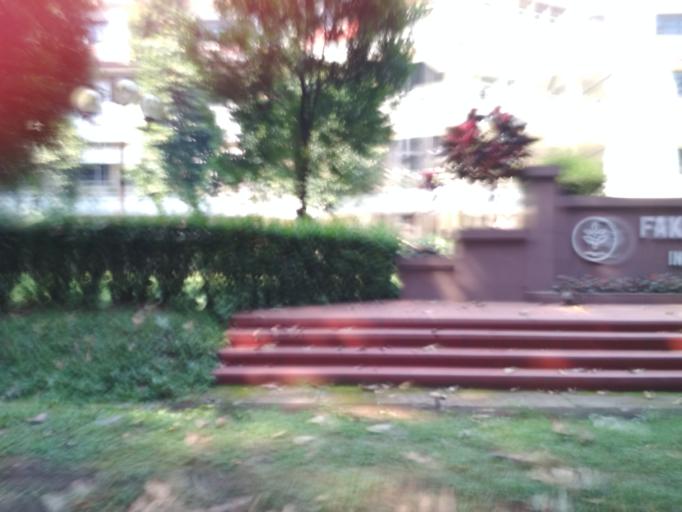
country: ID
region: West Java
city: Ciampea
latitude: -6.5568
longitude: 106.7229
